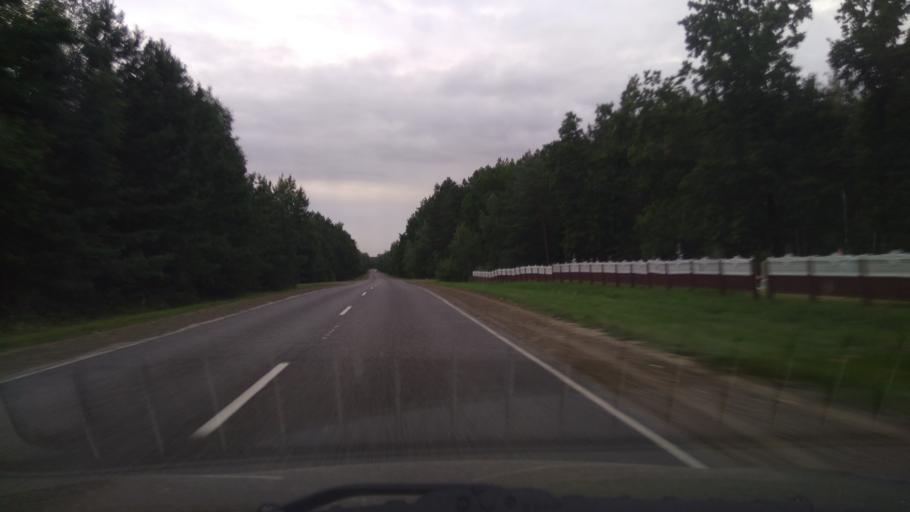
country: BY
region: Brest
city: Byaroza
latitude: 52.4055
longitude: 24.9996
